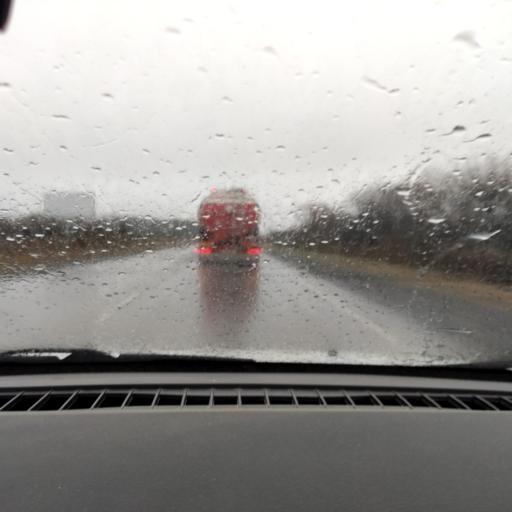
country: RU
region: Perm
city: Froly
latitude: 57.8995
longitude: 56.2289
